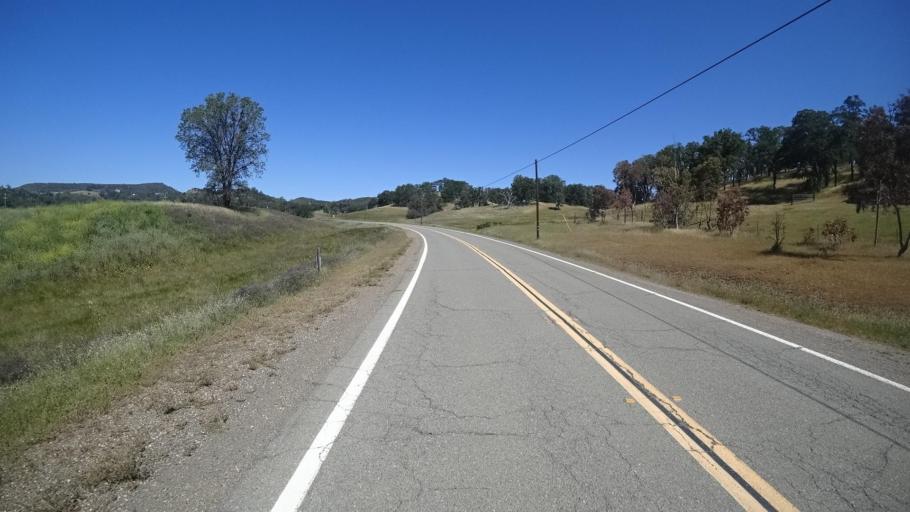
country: US
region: California
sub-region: Lake County
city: Hidden Valley Lake
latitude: 38.8699
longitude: -122.4171
